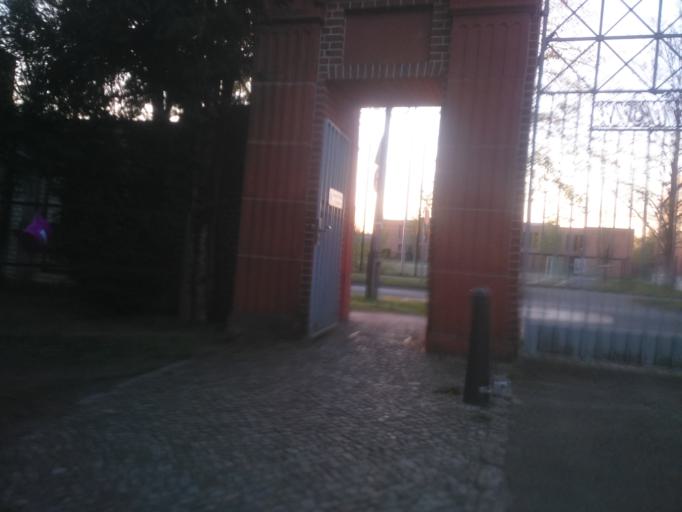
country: DE
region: Berlin
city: Weissensee
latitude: 52.5573
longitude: 13.4519
